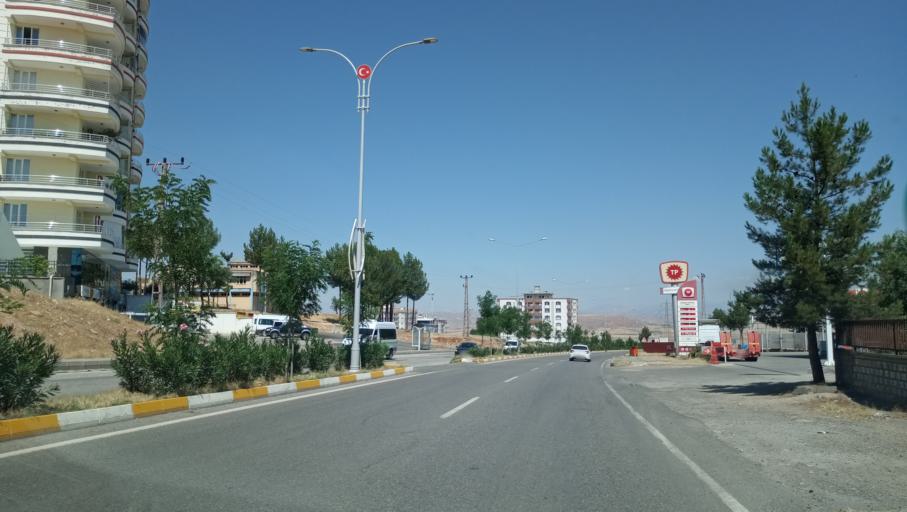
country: TR
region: Siirt
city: Civankan
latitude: 37.9502
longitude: 41.8918
